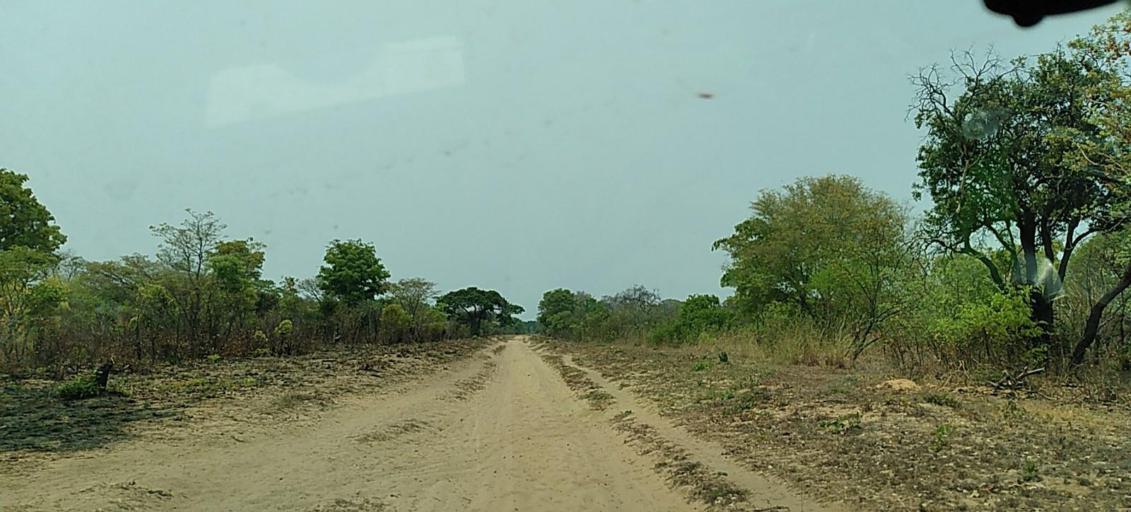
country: ZM
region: Western
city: Lukulu
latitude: -14.1518
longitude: 23.2991
